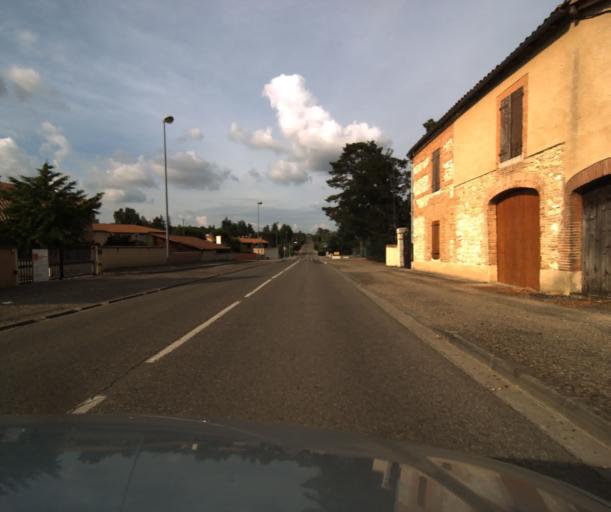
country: FR
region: Midi-Pyrenees
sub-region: Departement du Tarn-et-Garonne
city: Beaumont-de-Lomagne
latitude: 43.8764
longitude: 0.9776
